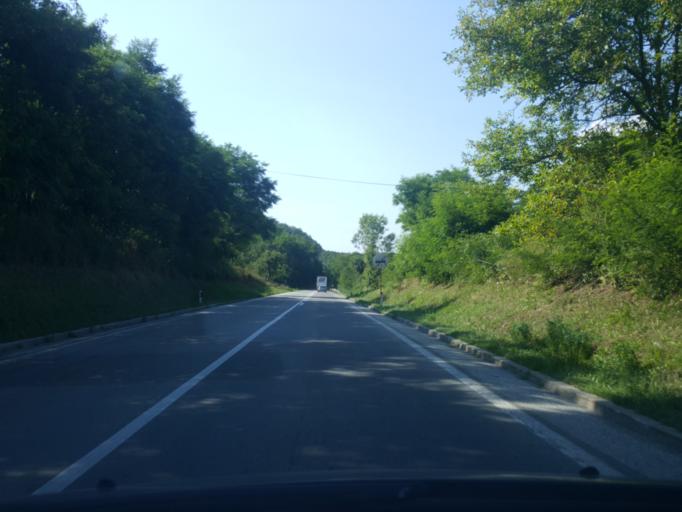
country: RS
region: Central Serbia
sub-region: Moravicki Okrug
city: Gornji Milanovac
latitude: 44.0737
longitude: 20.4884
